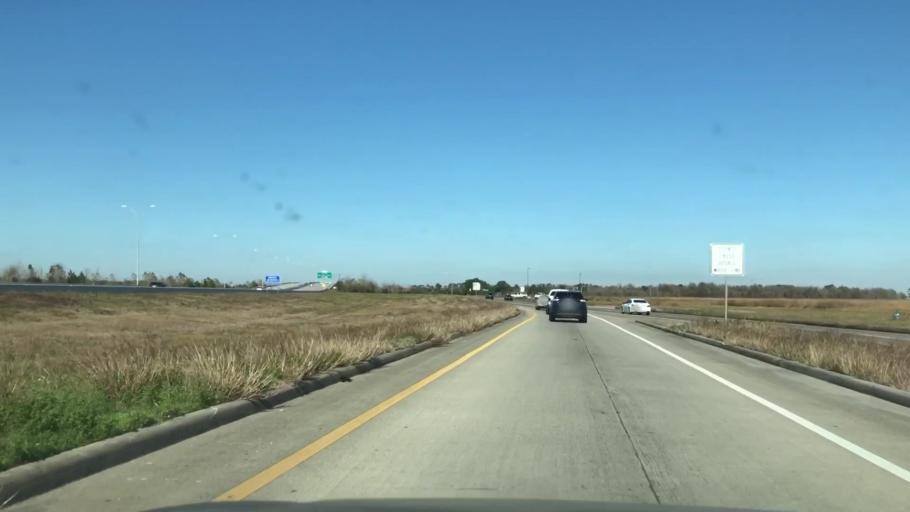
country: US
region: Texas
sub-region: Harris County
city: Cloverleaf
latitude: 29.8260
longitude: -95.1689
